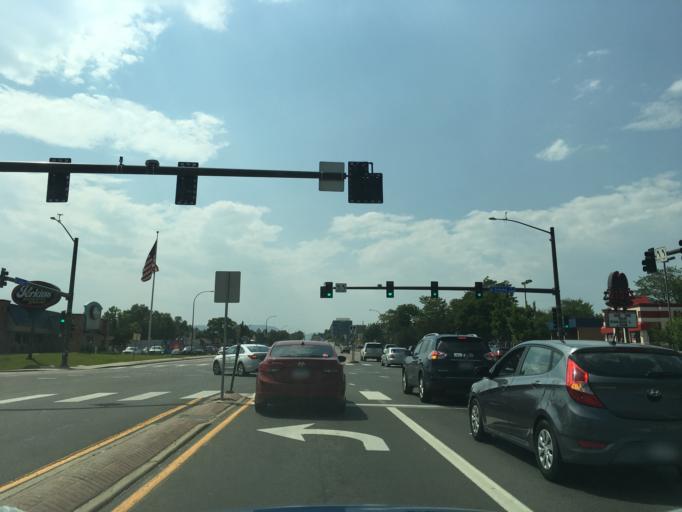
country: US
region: Colorado
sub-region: Jefferson County
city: Applewood
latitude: 39.7402
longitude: -105.1279
